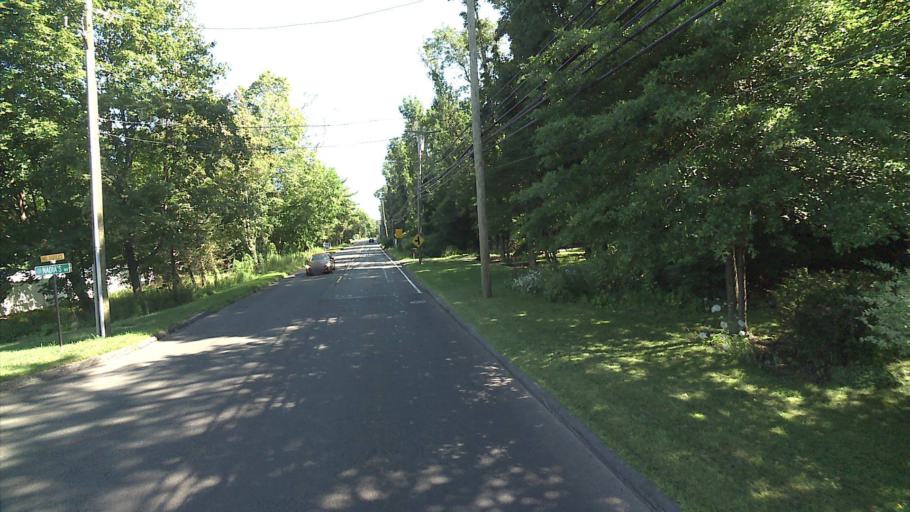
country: US
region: Connecticut
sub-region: Hartford County
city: Farmington
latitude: 41.7013
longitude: -72.8439
